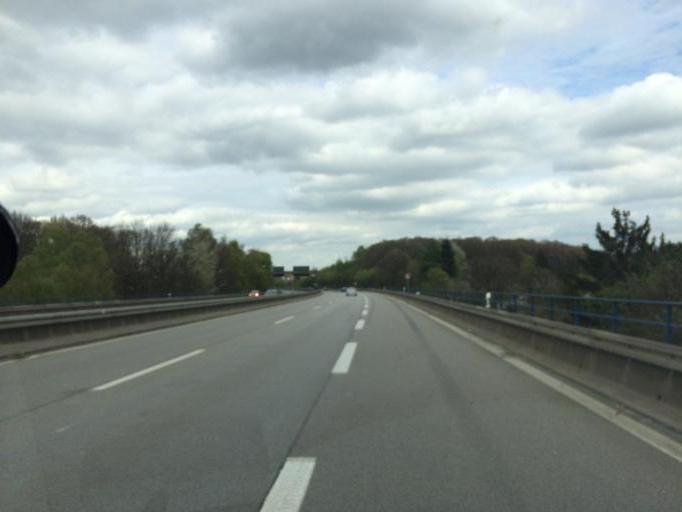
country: DE
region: North Rhine-Westphalia
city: Sprockhovel
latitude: 51.3184
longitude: 7.2679
